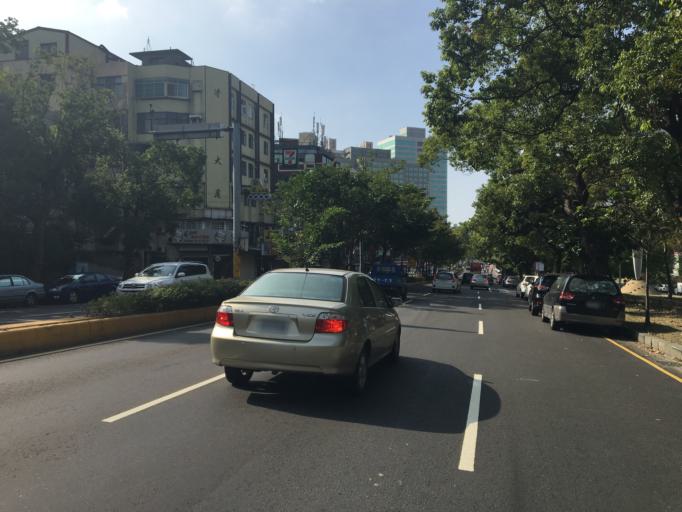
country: TW
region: Taiwan
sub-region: Hsinchu
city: Hsinchu
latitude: 24.7992
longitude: 120.9931
